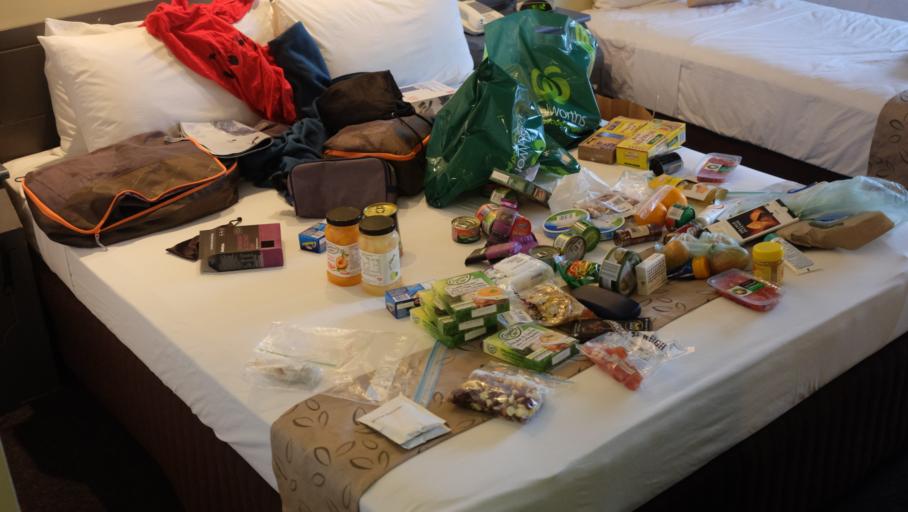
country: AU
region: Northern Territory
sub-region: Alice Springs
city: Alice Springs
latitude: -23.6997
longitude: 133.8839
